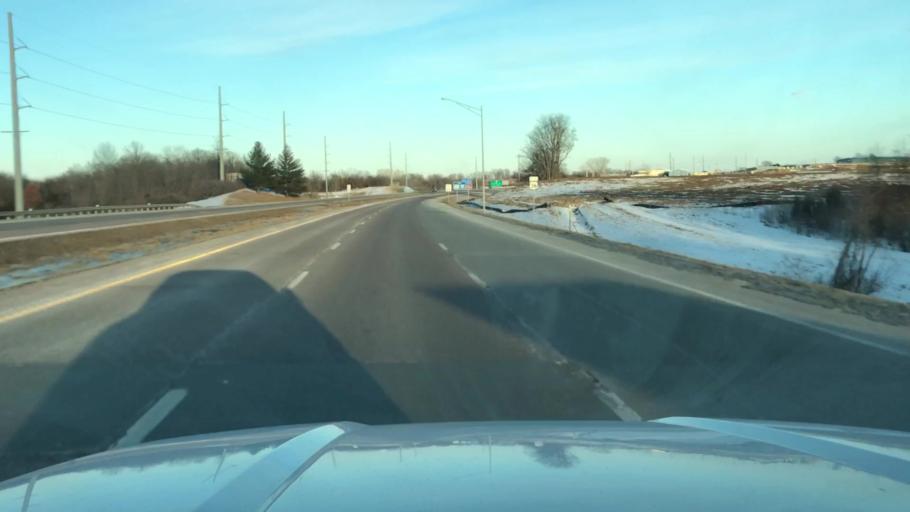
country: US
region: Missouri
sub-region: Buchanan County
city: Saint Joseph
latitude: 39.7507
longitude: -94.7851
